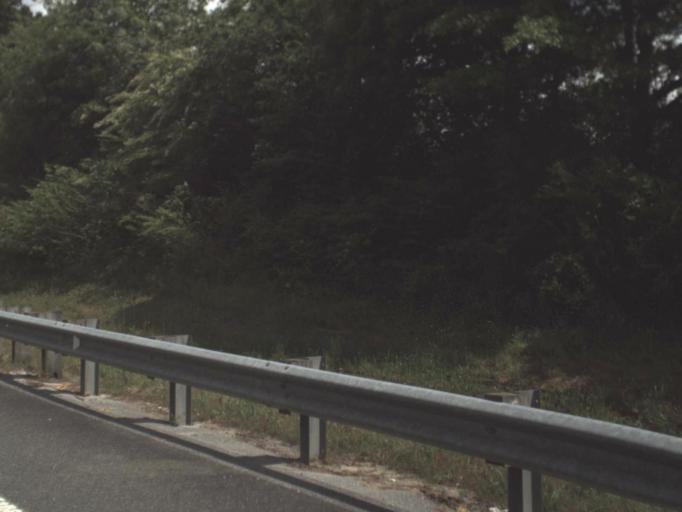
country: US
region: Florida
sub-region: Santa Rosa County
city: Point Baker
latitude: 30.8067
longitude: -87.1150
